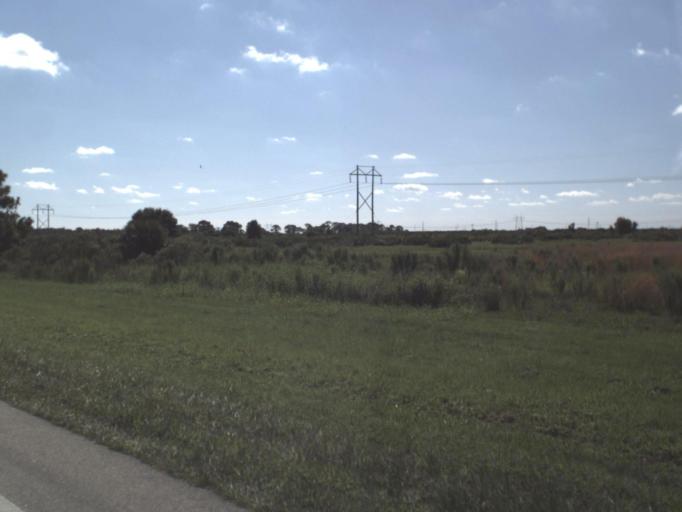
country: US
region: Florida
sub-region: Collier County
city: Immokalee
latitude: 26.4968
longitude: -81.4786
